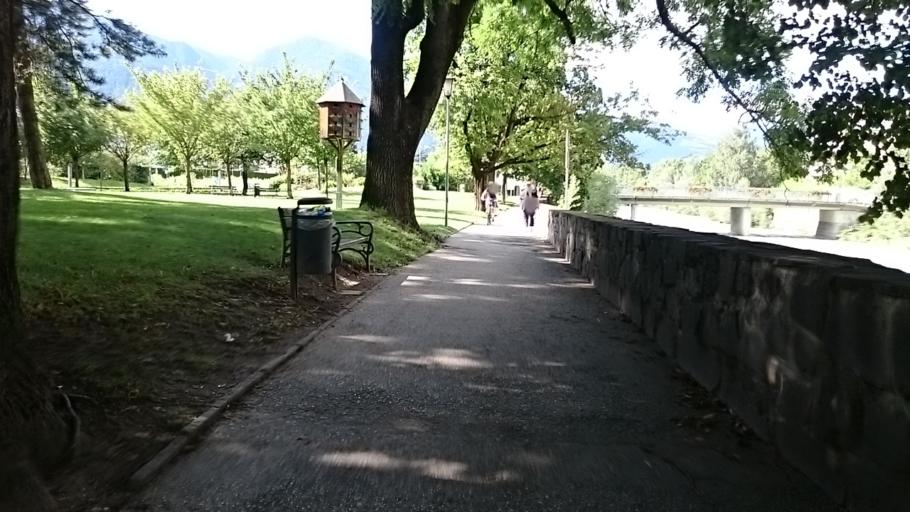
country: IT
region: Trentino-Alto Adige
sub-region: Bolzano
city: Bressanone
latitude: 46.7224
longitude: 11.6563
